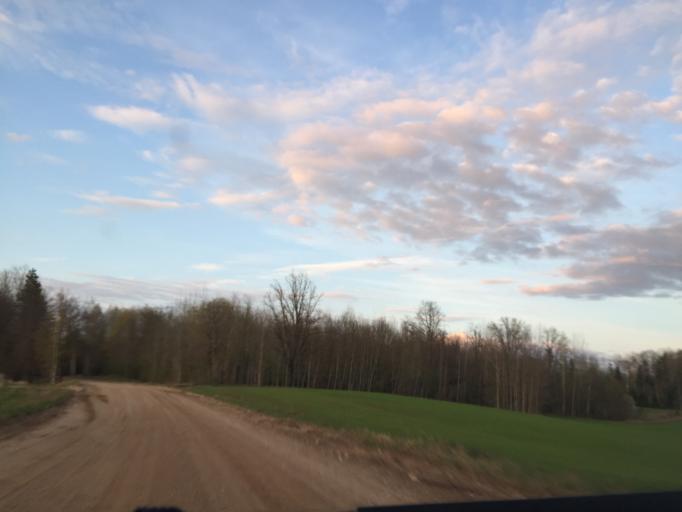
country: LV
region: Gulbenes Rajons
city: Gulbene
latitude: 57.2525
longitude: 26.9082
